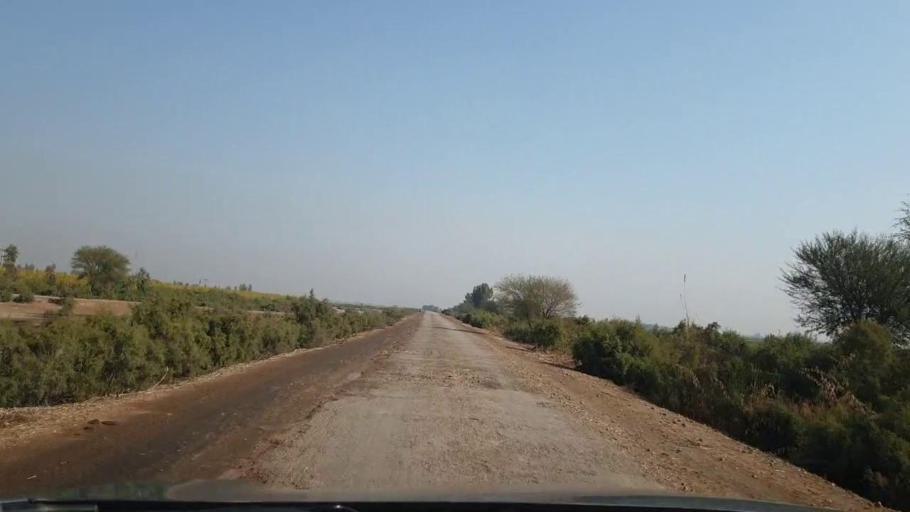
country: PK
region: Sindh
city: Berani
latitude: 25.6360
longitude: 68.8667
